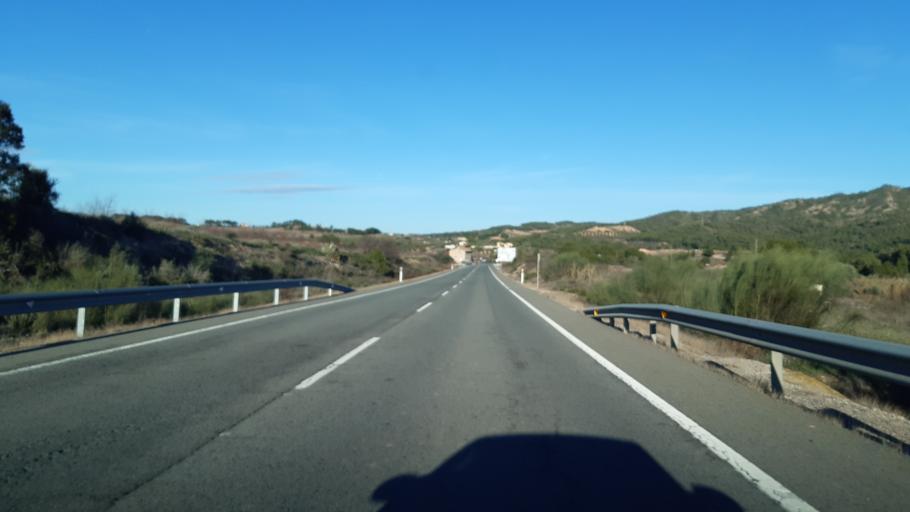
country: ES
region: Catalonia
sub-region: Provincia de Tarragona
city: la Fatarella
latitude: 41.1062
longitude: 0.5276
